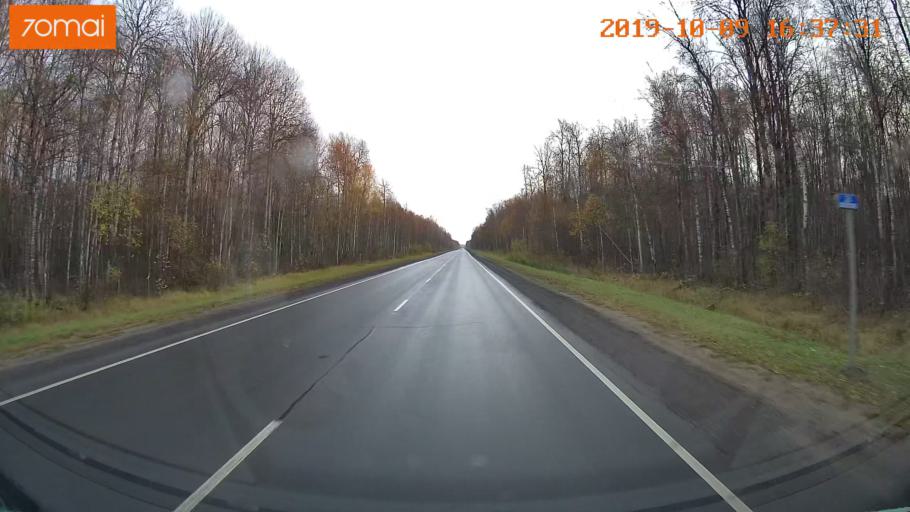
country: RU
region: Kostroma
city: Volgorechensk
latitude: 57.5258
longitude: 41.0256
